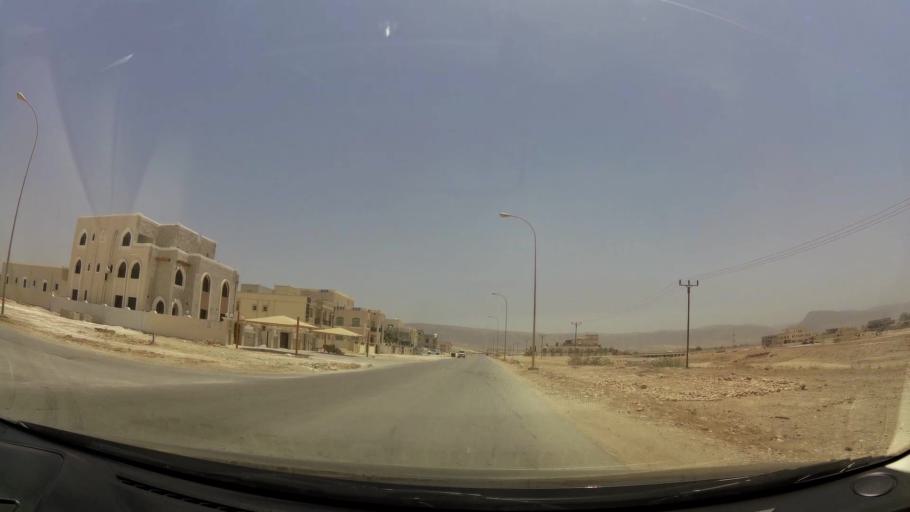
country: OM
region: Zufar
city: Salalah
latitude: 17.0953
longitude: 54.1592
